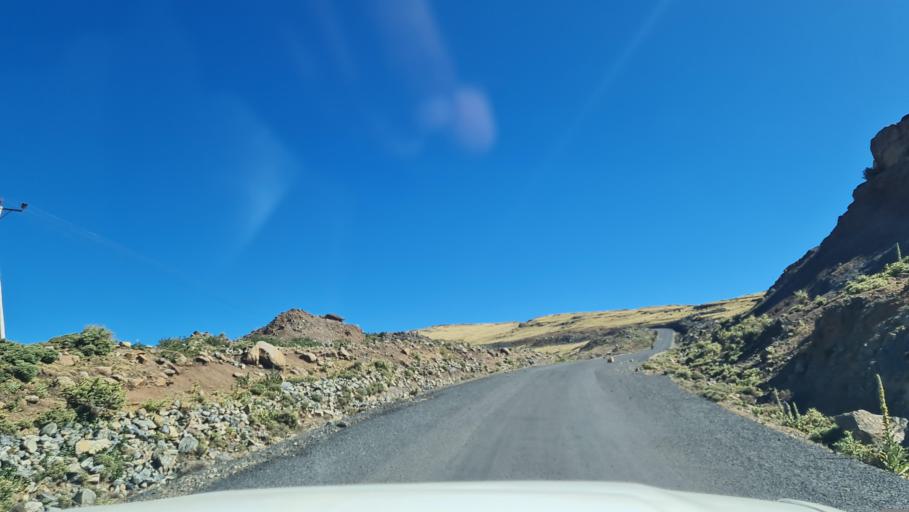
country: ET
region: Amhara
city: Debark'
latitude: 13.1473
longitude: 38.1830
